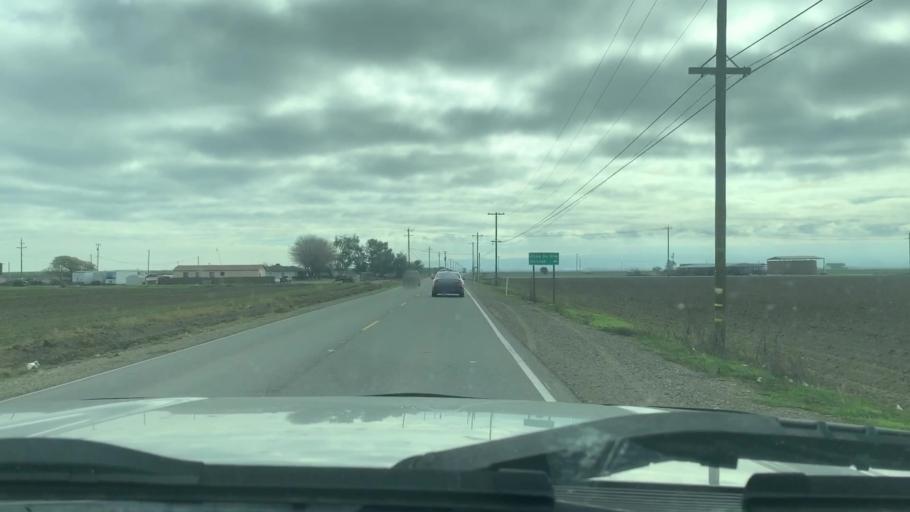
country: US
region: California
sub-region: Merced County
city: Los Banos
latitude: 37.0294
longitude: -120.8361
